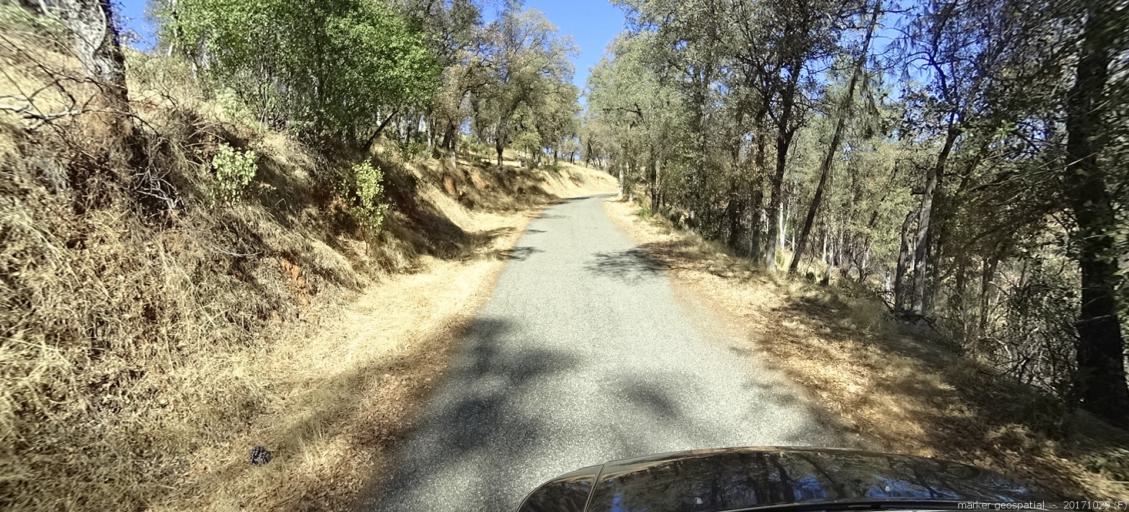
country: US
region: California
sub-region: Shasta County
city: Shasta
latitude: 40.4795
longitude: -122.6243
